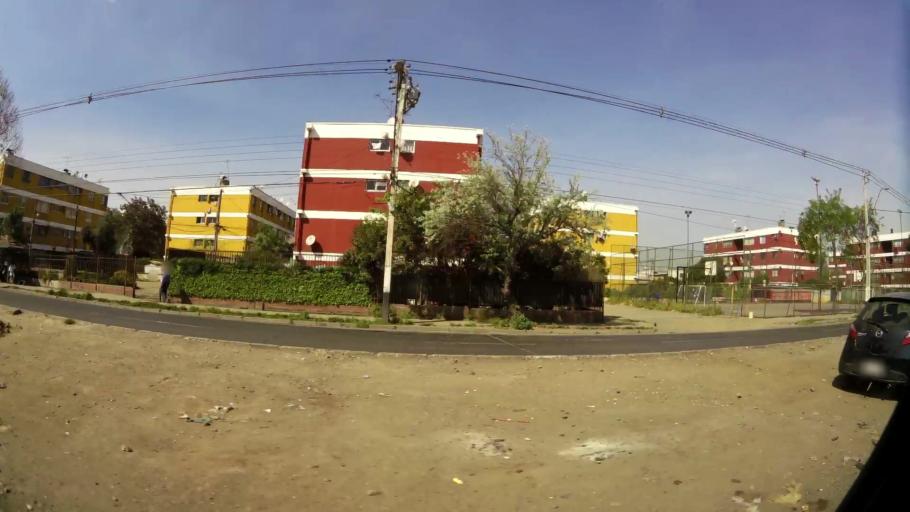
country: CL
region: Santiago Metropolitan
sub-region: Provincia de Santiago
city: Lo Prado
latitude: -33.4300
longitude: -70.7439
